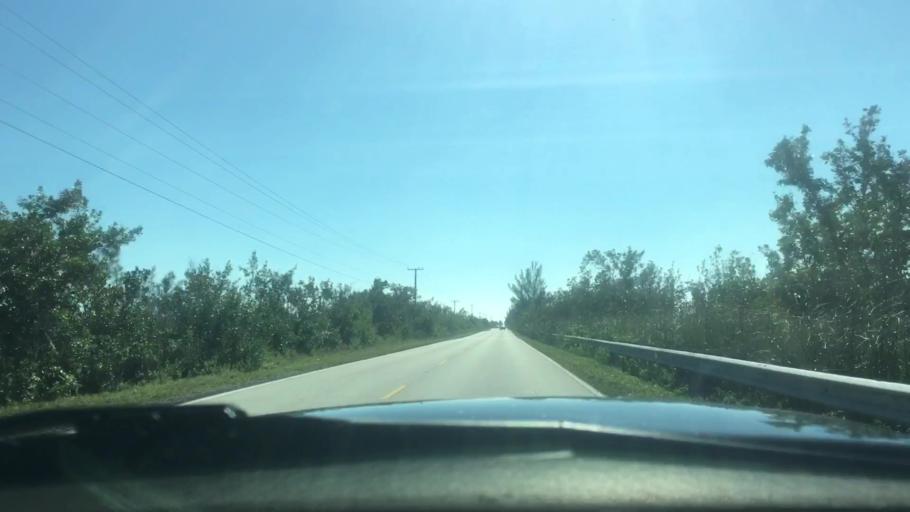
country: US
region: Florida
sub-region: Miami-Dade County
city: Florida City
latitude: 25.3612
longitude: -80.4261
